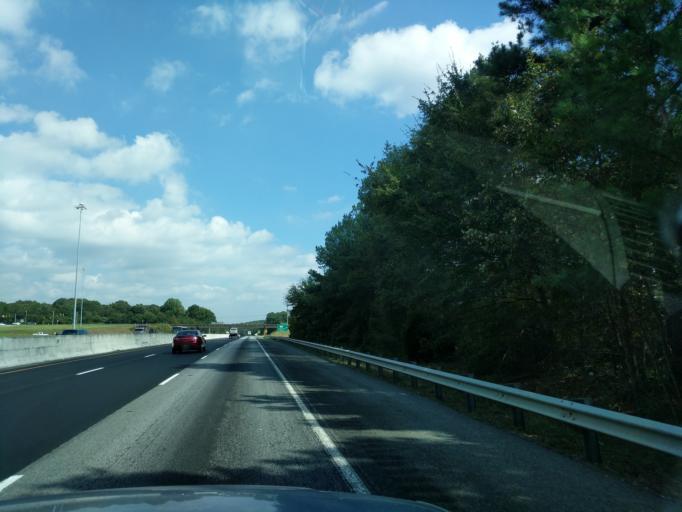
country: US
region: South Carolina
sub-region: Anderson County
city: Northlake
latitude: 34.5776
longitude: -82.6966
